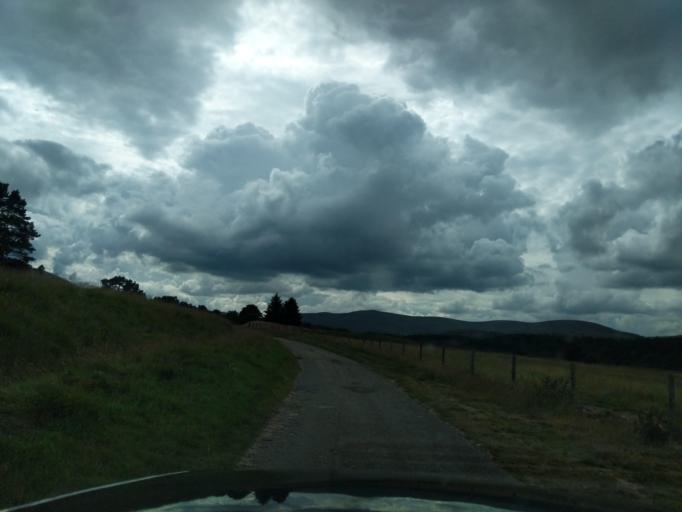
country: GB
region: Scotland
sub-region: Highland
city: Aviemore
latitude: 57.2571
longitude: -3.8976
